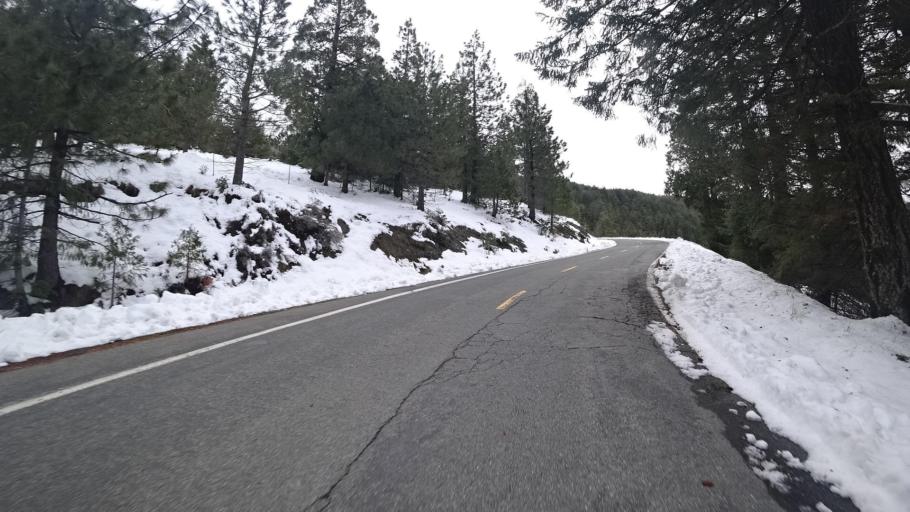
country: US
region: California
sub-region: Humboldt County
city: Willow Creek
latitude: 40.8640
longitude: -123.7405
